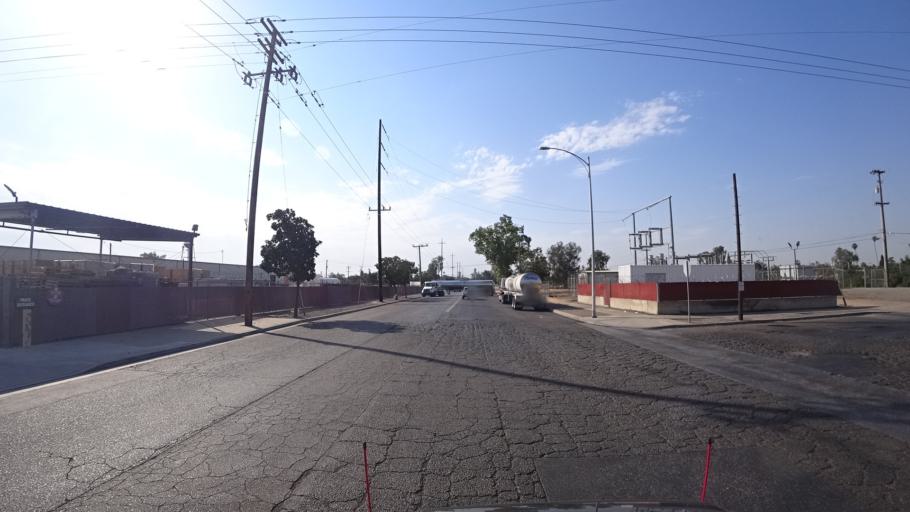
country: US
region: California
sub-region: Fresno County
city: Fresno
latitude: 36.7268
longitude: -119.7928
